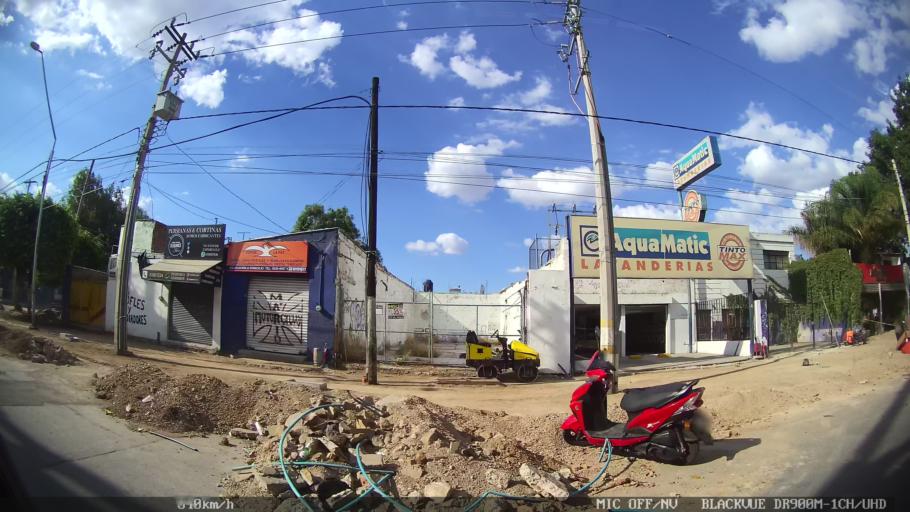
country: MX
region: Jalisco
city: Tlaquepaque
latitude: 20.6508
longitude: -103.3099
